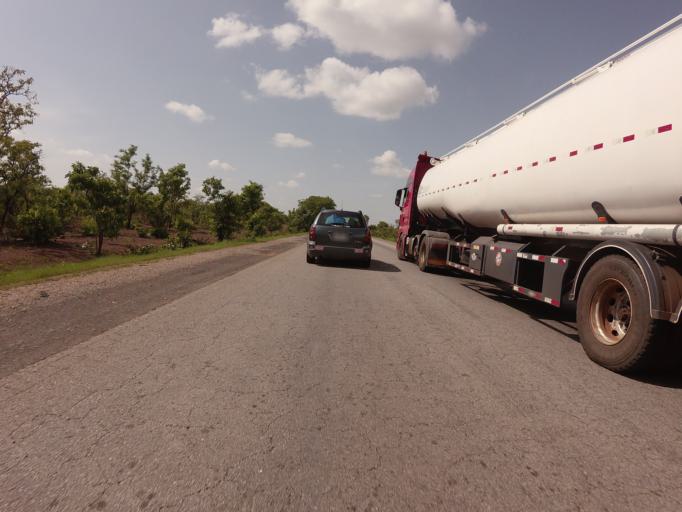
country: GH
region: Northern
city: Savelugu
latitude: 9.9574
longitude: -0.8339
